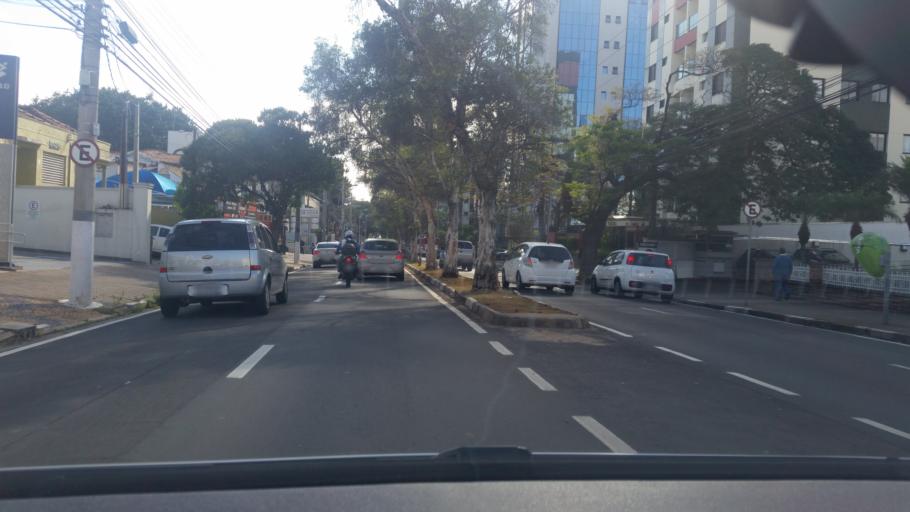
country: BR
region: Sao Paulo
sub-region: Campinas
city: Campinas
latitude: -22.8964
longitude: -47.0675
